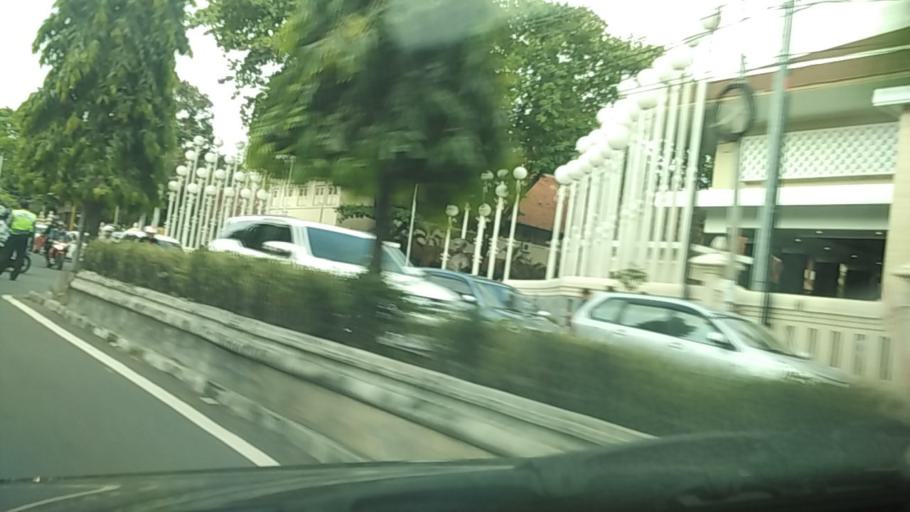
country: ID
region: Daerah Istimewa Yogyakarta
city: Yogyakarta
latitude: -7.7757
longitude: 110.3890
